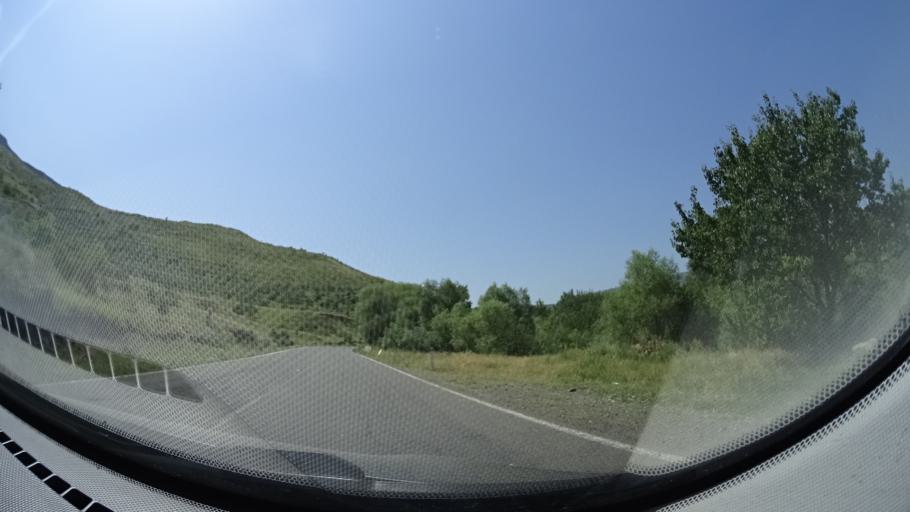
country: GE
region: Samtskhe-Javakheti
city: Aspindza
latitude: 41.5294
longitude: 43.2606
